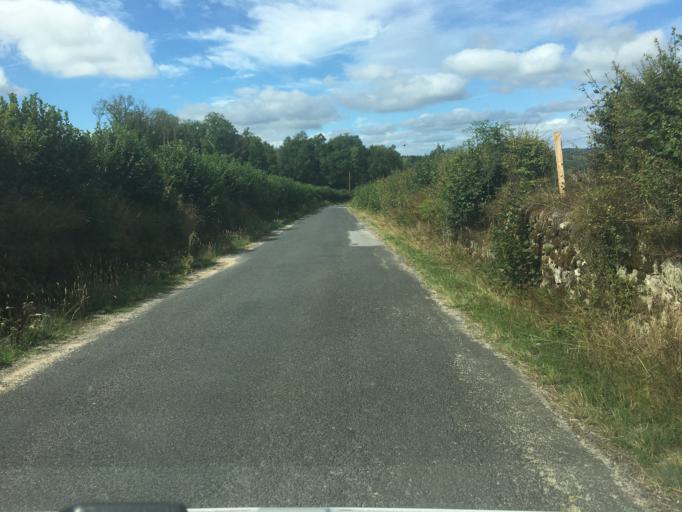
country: FR
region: Auvergne
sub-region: Departement du Cantal
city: Champagnac
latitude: 45.4352
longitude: 2.4086
